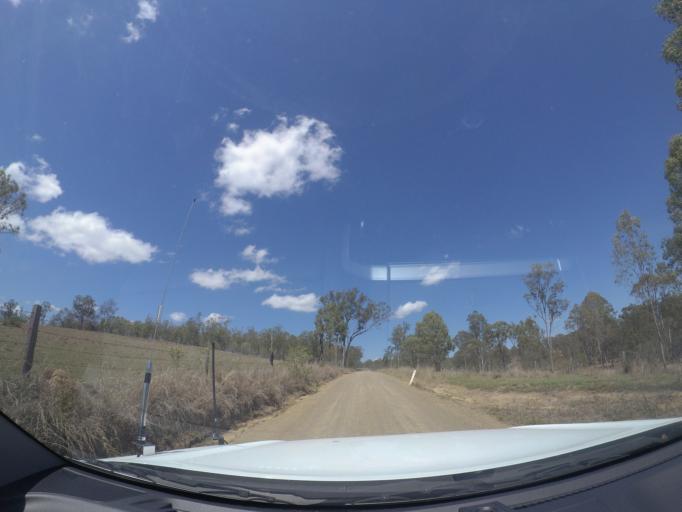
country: AU
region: Queensland
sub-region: Logan
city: Cedar Vale
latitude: -27.8548
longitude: 152.8852
